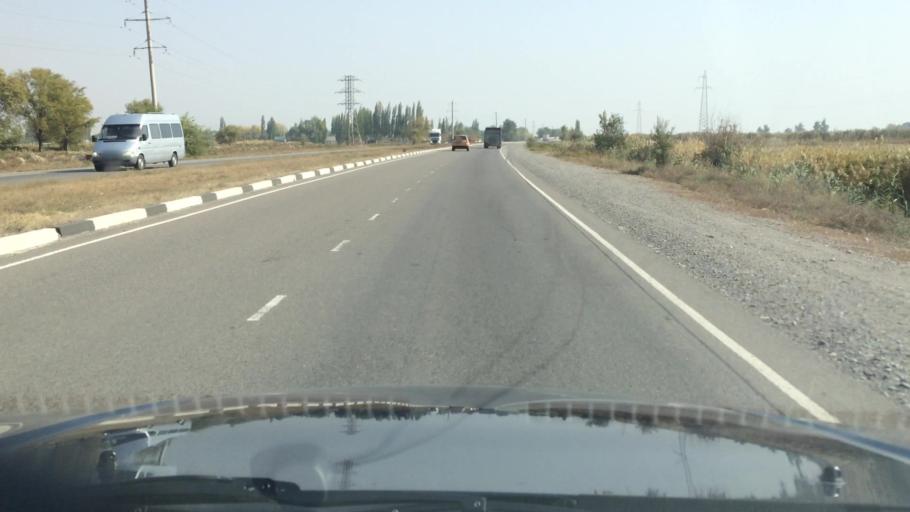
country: KG
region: Chuy
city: Kant
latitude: 42.9670
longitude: 74.8252
